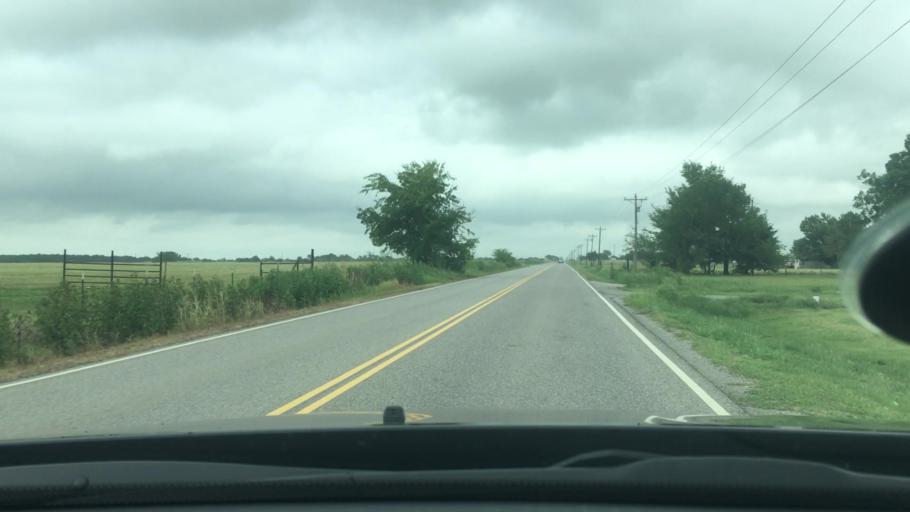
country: US
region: Oklahoma
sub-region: Bryan County
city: Colbert
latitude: 33.9034
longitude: -96.5006
